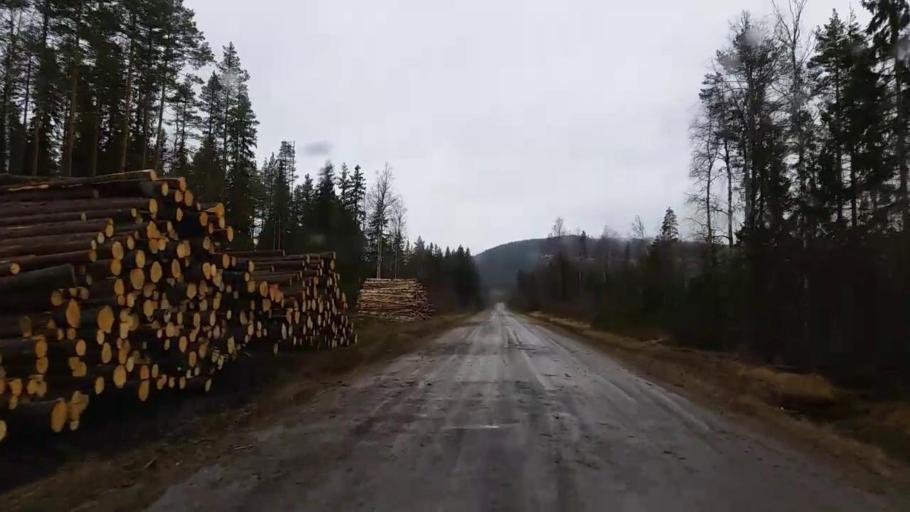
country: SE
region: Gaevleborg
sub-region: Ljusdals Kommun
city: Farila
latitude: 62.0749
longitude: 15.7768
